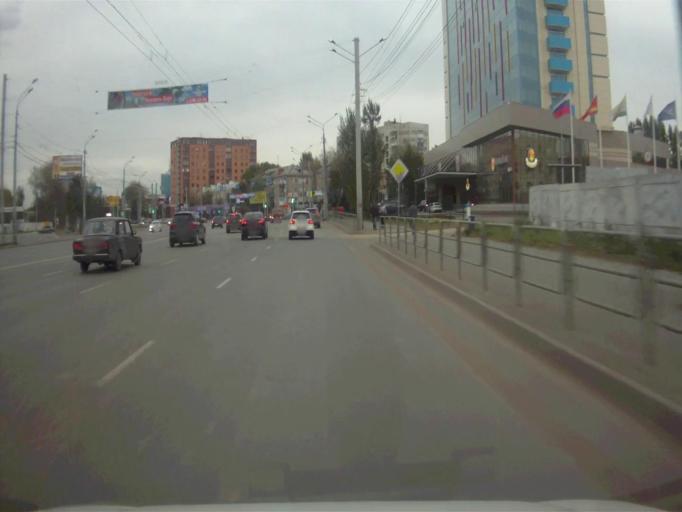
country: RU
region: Chelyabinsk
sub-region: Gorod Chelyabinsk
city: Chelyabinsk
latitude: 55.1681
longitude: 61.3783
